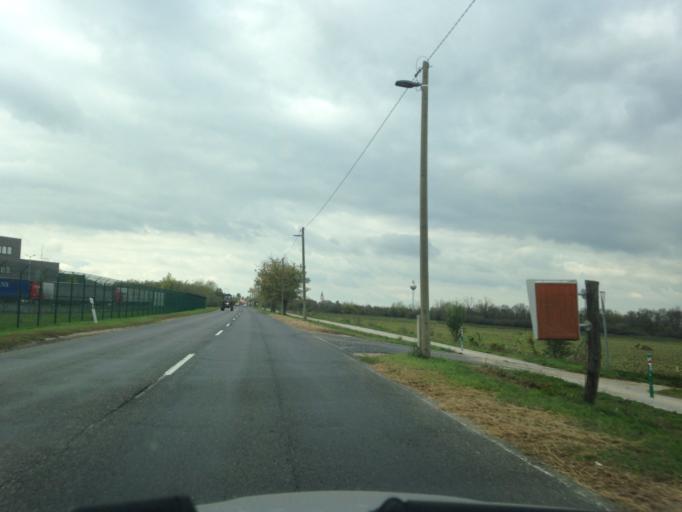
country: HU
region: Gyor-Moson-Sopron
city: Rajka
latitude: 47.9091
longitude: 17.1766
